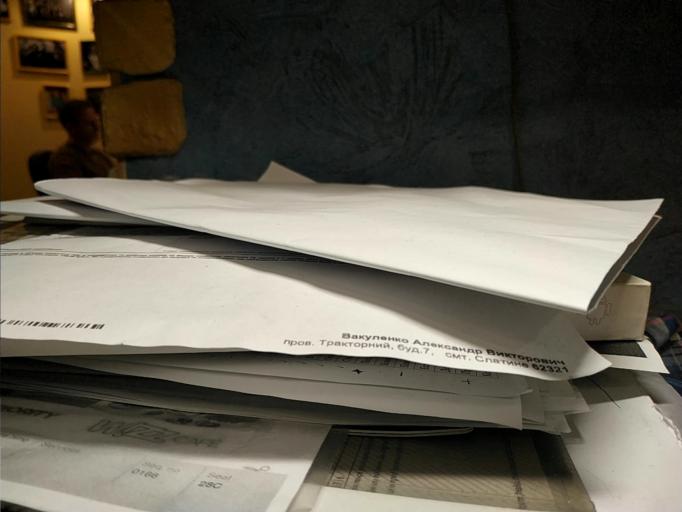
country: RU
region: Tverskaya
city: Zubtsov
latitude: 56.1081
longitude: 34.6427
